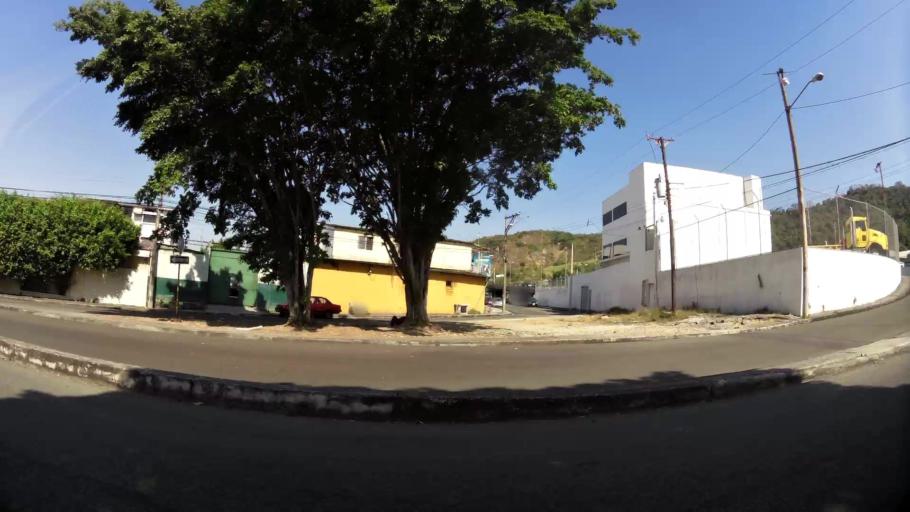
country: EC
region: Guayas
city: Guayaquil
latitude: -2.1654
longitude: -79.9222
